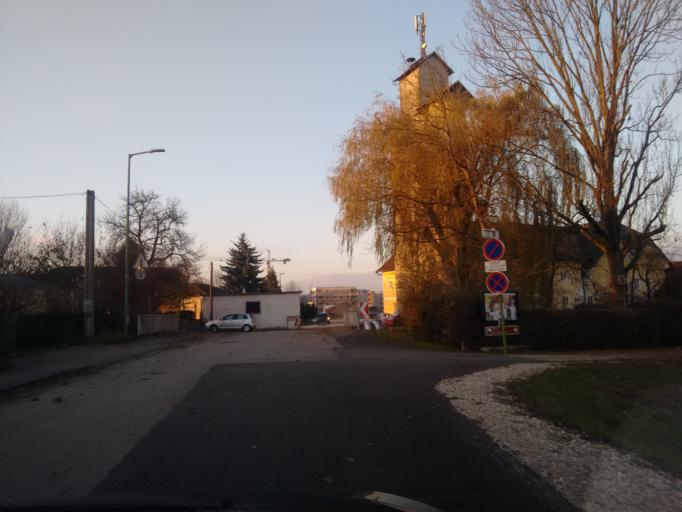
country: AT
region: Upper Austria
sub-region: Wels Stadt
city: Wels
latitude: 48.1702
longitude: 13.9998
